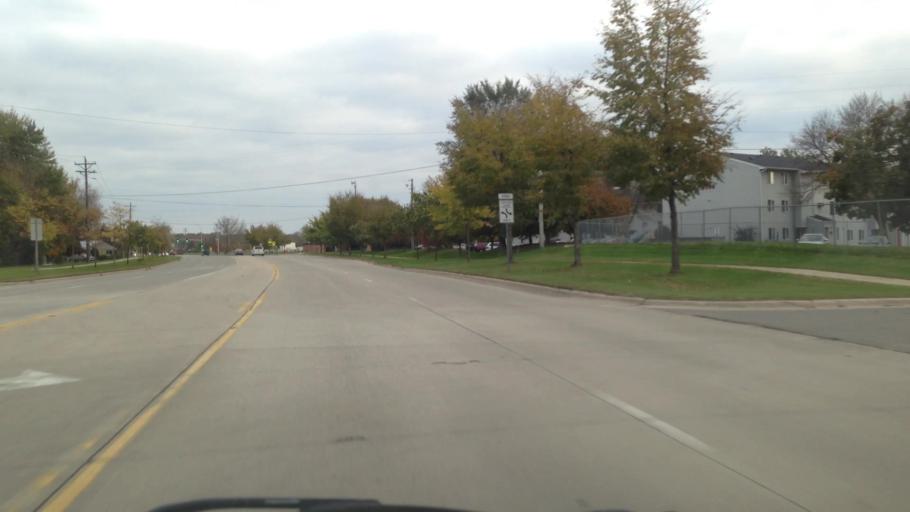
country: US
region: Minnesota
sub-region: Olmsted County
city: Rochester
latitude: 44.0018
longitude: -92.4368
